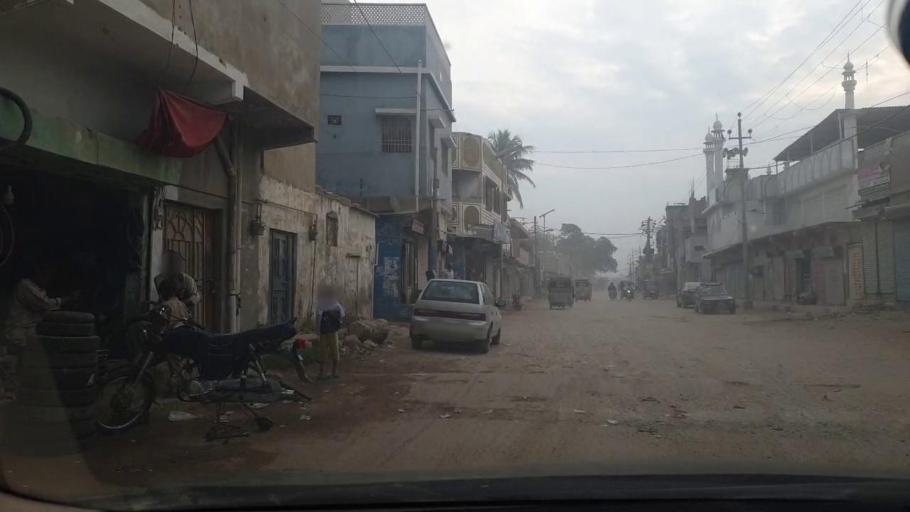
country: PK
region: Sindh
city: Malir Cantonment
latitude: 24.8791
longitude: 67.1953
